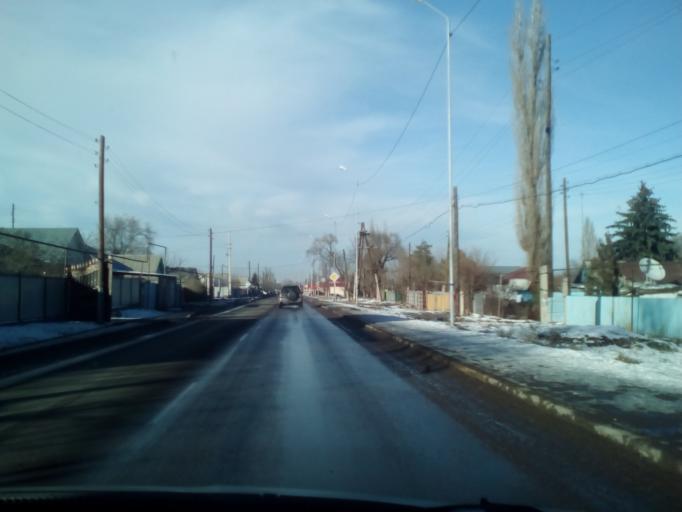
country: KZ
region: Almaty Oblysy
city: Burunday
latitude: 43.1700
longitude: 76.4161
